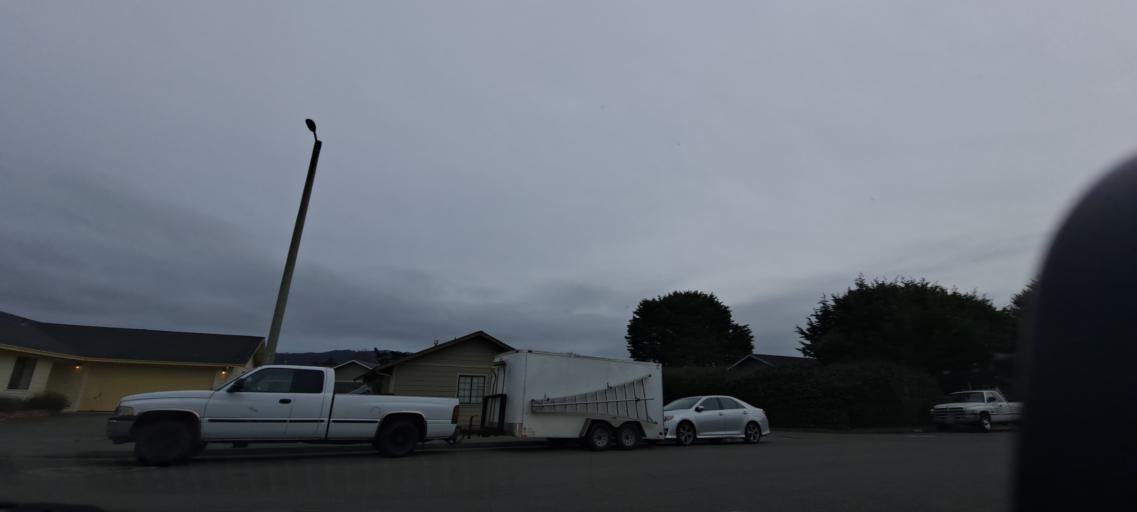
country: US
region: California
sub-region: Humboldt County
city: Arcata
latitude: 40.8725
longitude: -124.1013
